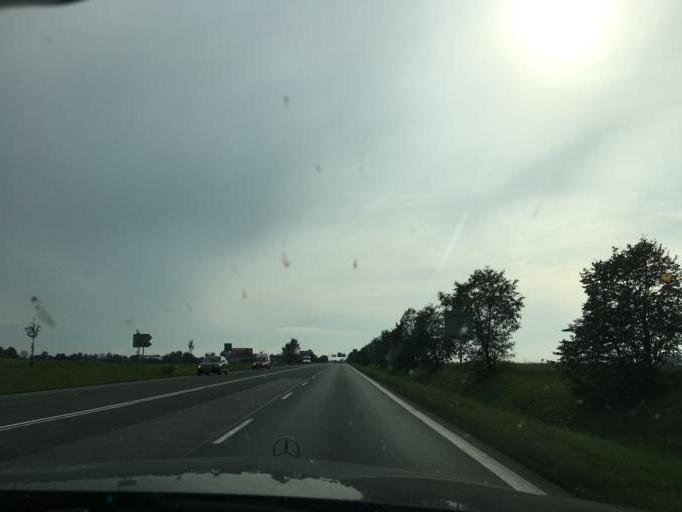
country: CZ
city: Stezery
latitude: 50.2092
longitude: 15.7814
